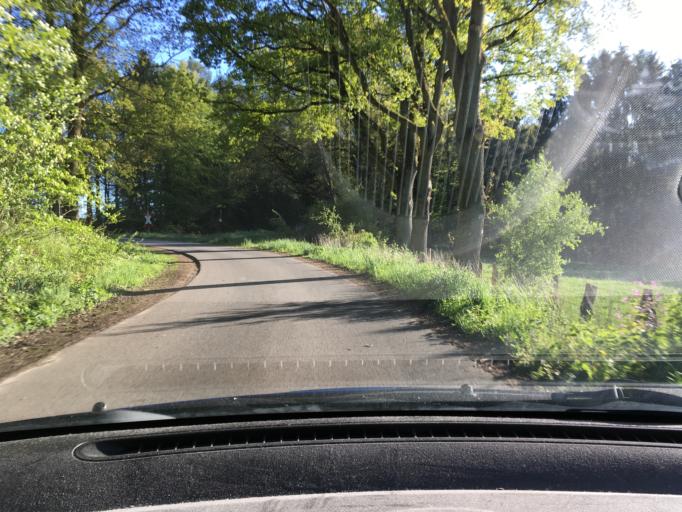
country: DE
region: Lower Saxony
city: Soderstorf
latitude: 53.1367
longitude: 10.1452
